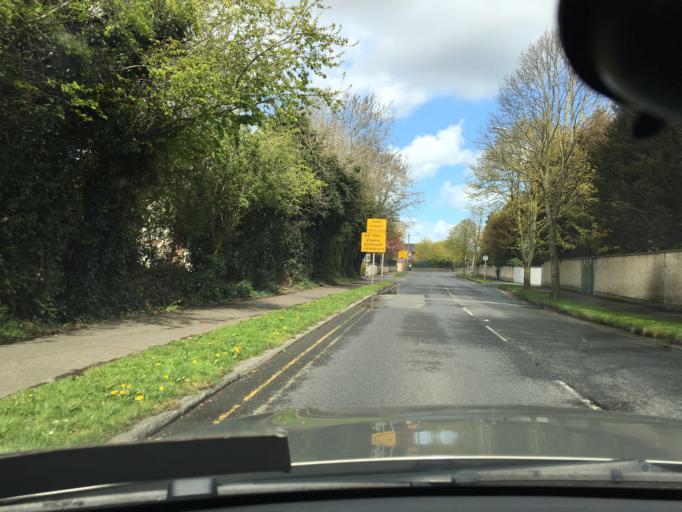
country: IE
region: Leinster
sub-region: Fingal County
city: Blanchardstown
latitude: 53.3759
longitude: -6.3914
